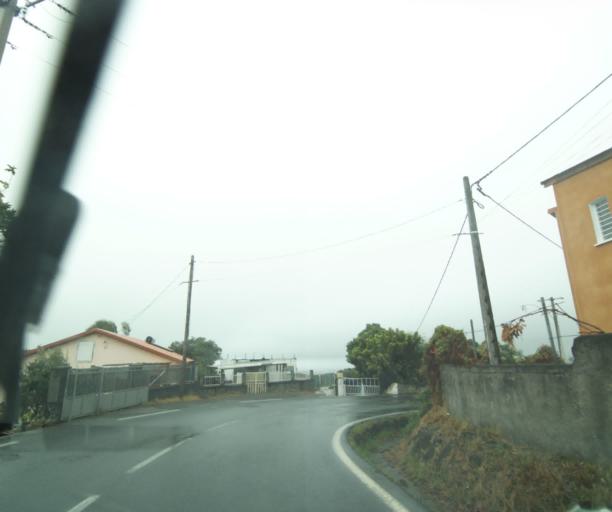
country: RE
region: Reunion
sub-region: Reunion
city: Saint-Paul
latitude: -21.0257
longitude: 55.2866
